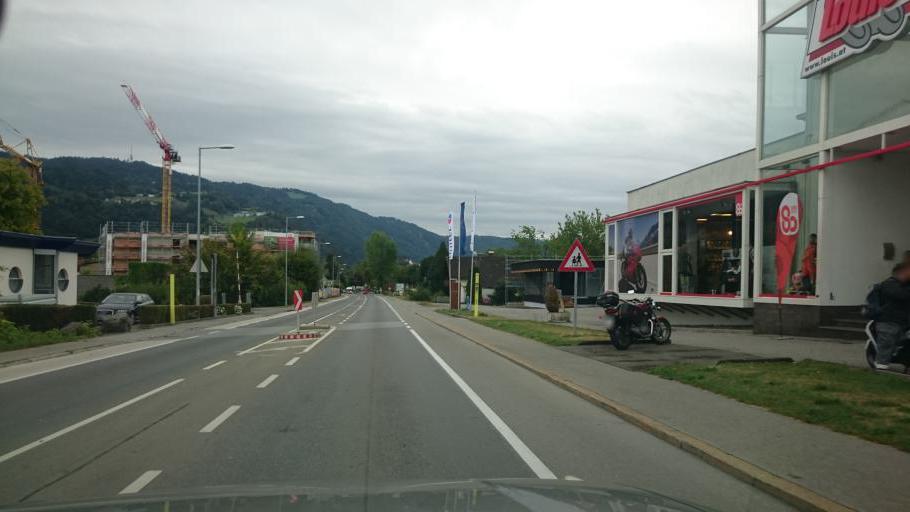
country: AT
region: Vorarlberg
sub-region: Politischer Bezirk Bregenz
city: Lochau
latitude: 47.5327
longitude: 9.7405
